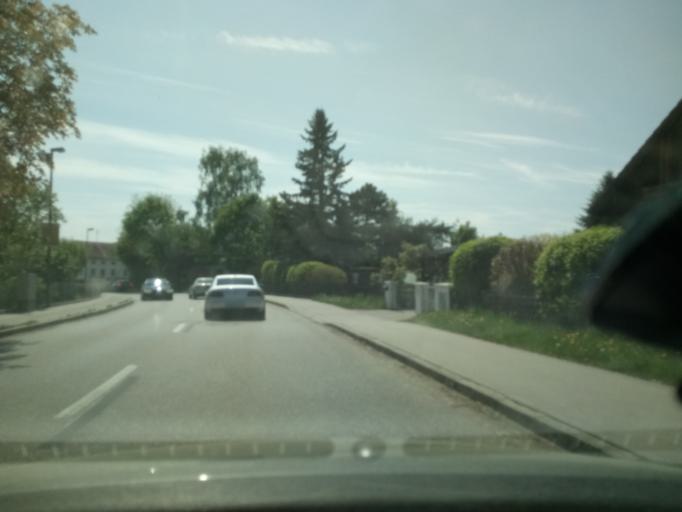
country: DE
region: Bavaria
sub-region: Upper Bavaria
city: Kraiburg am Inn
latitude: 48.2027
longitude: 12.4233
